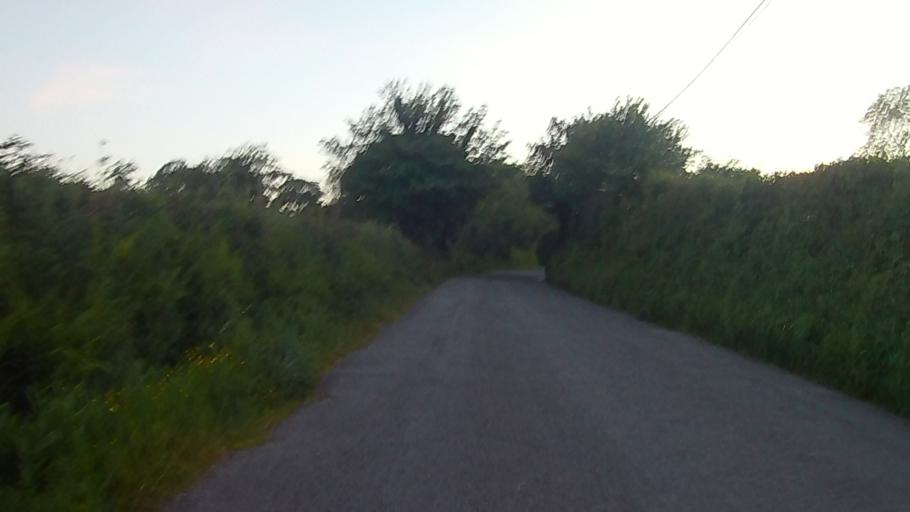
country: IE
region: Munster
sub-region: County Cork
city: Midleton
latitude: 51.9727
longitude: -8.2249
